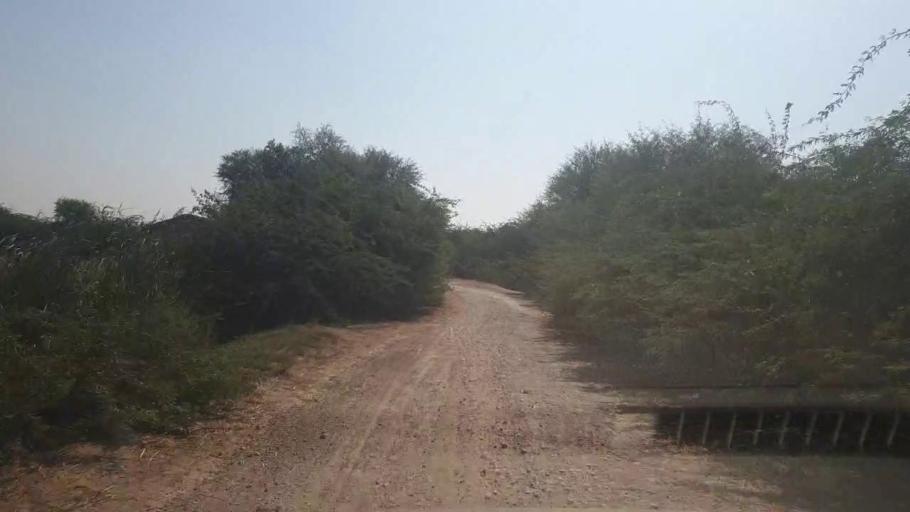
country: PK
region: Sindh
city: Badin
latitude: 24.5835
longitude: 68.8453
